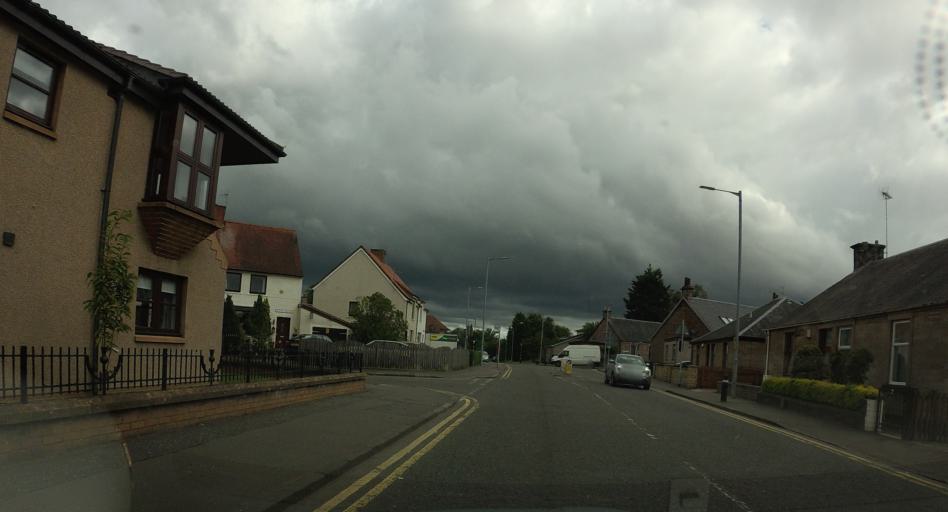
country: GB
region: Scotland
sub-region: Clackmannanshire
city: Alloa
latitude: 56.1266
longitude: -3.7850
